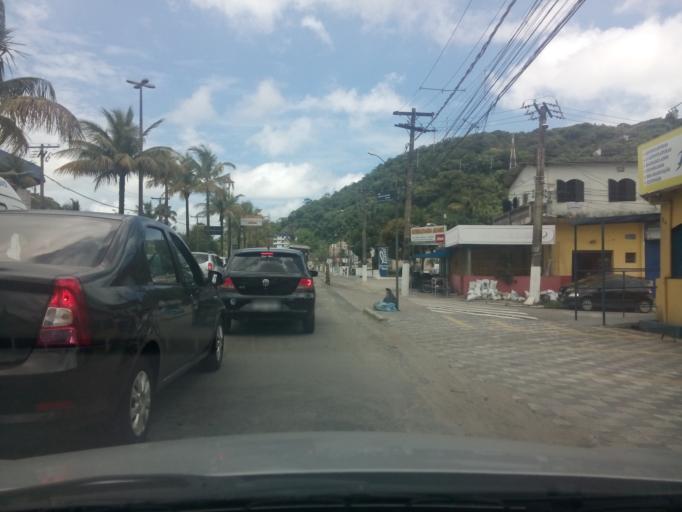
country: BR
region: Sao Paulo
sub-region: Guaruja
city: Guaruja
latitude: -23.9867
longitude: -46.2654
